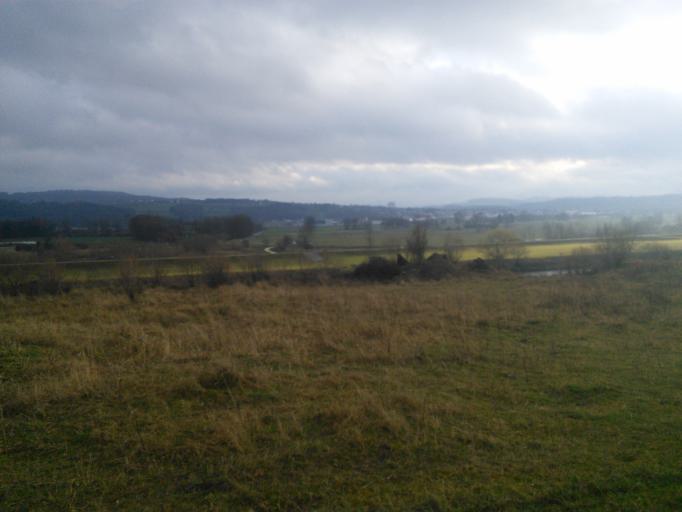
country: CH
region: Thurgau
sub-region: Frauenfeld District
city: Frauenfeld
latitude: 47.5875
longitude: 8.9146
